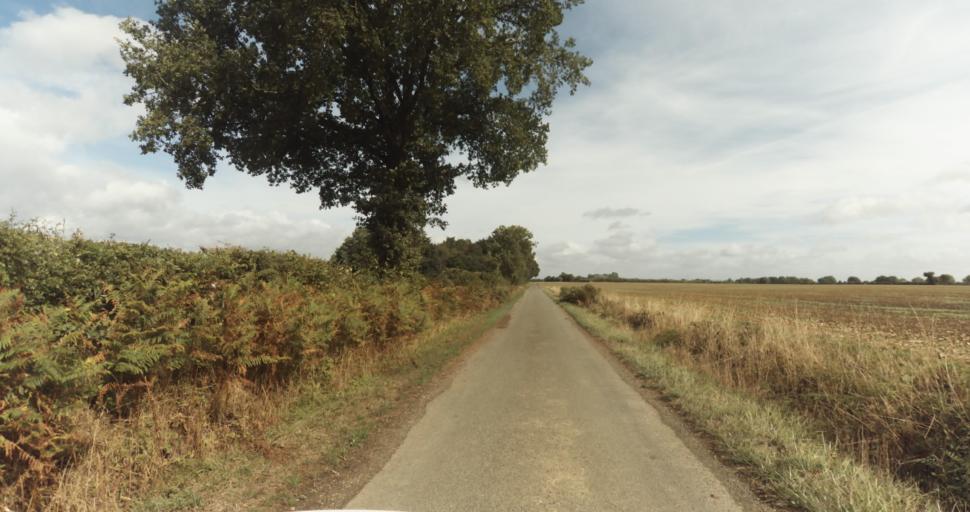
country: FR
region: Lower Normandy
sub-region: Departement de l'Orne
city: Gace
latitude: 48.8293
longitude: 0.3940
